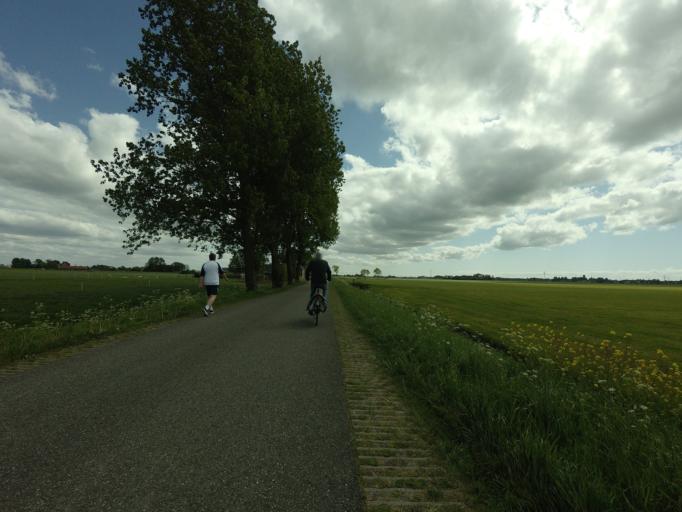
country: NL
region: Friesland
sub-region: Sudwest Fryslan
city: Bolsward
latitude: 53.0811
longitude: 5.5510
